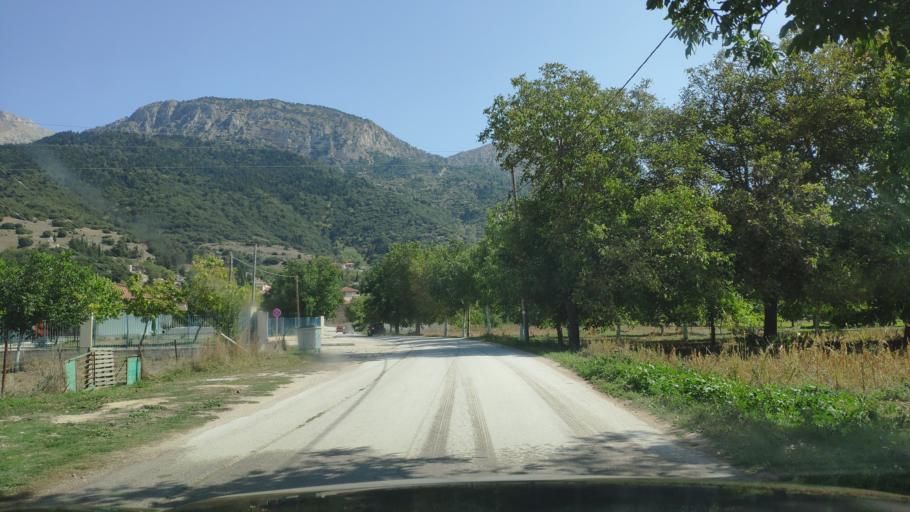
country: GR
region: West Greece
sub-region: Nomos Achaias
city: Aiyira
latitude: 37.9087
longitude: 22.3269
